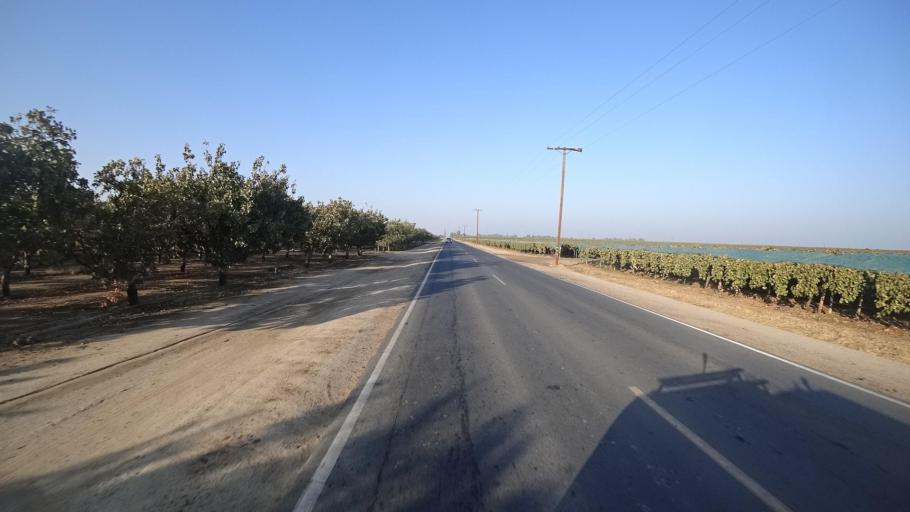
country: US
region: California
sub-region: Kern County
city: Delano
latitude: 35.7905
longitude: -119.2077
